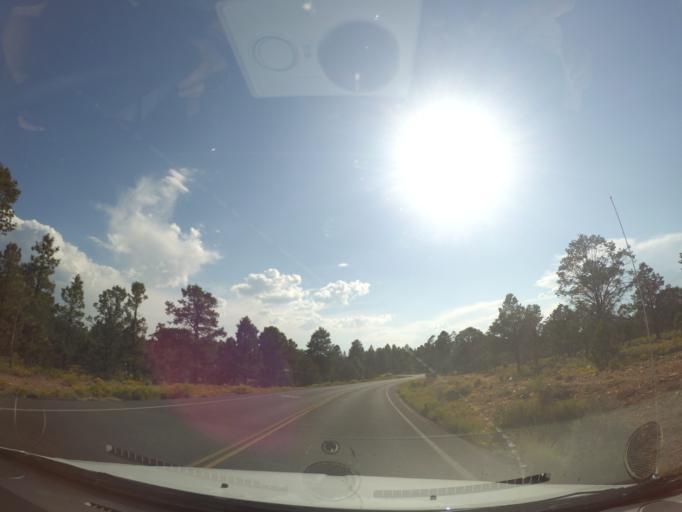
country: US
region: Arizona
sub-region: Coconino County
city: Grand Canyon
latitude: 36.0574
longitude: -112.1137
